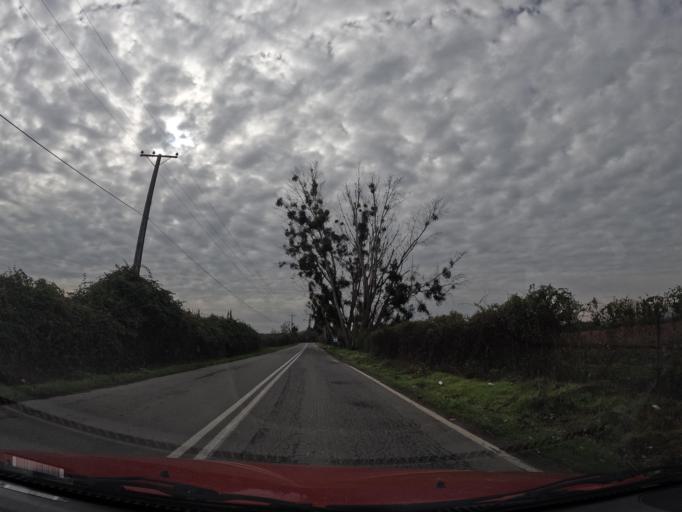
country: CL
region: Maule
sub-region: Provincia de Linares
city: Linares
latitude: -35.8576
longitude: -71.6157
